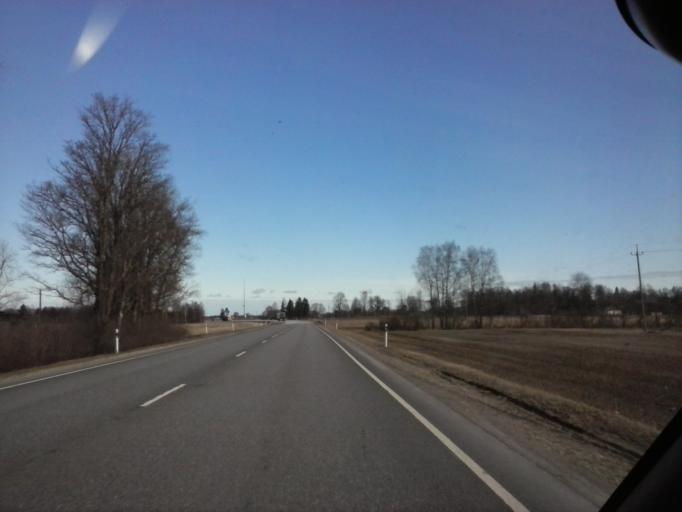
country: EE
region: Harju
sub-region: Anija vald
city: Kehra
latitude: 59.1372
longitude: 25.3189
